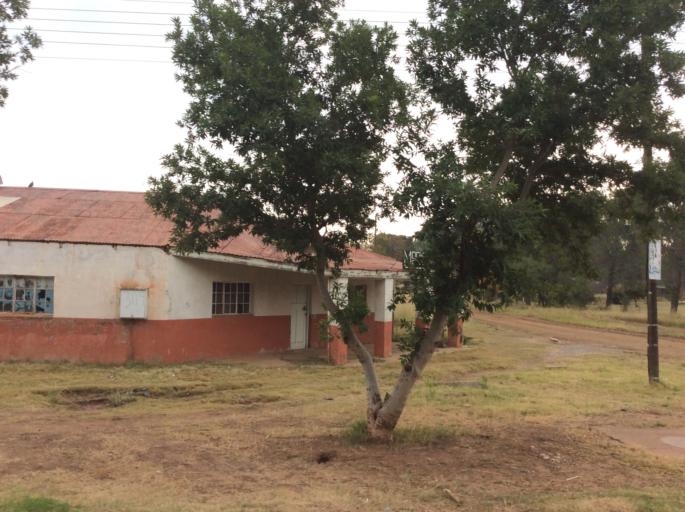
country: LS
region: Mafeteng
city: Mafeteng
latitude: -29.9872
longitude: 27.0156
